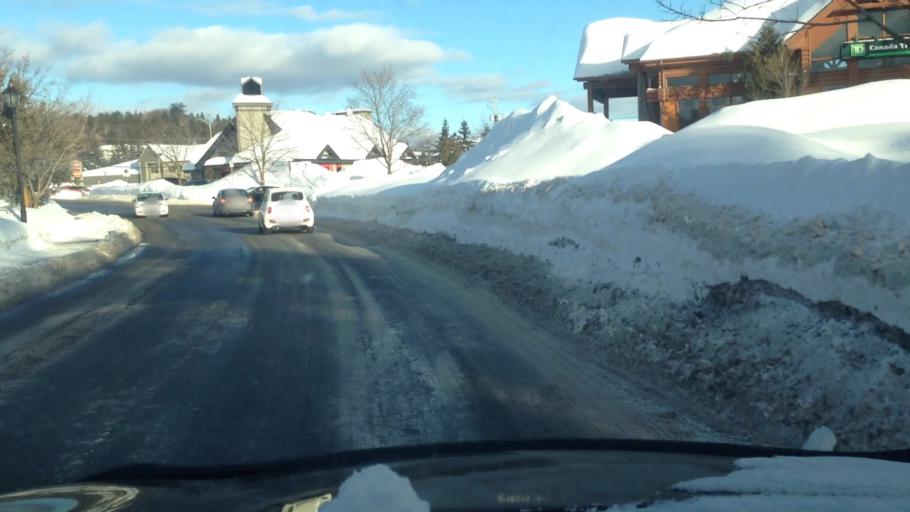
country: CA
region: Quebec
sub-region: Laurentides
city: Saint-Sauveur
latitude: 45.8898
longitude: -74.1500
